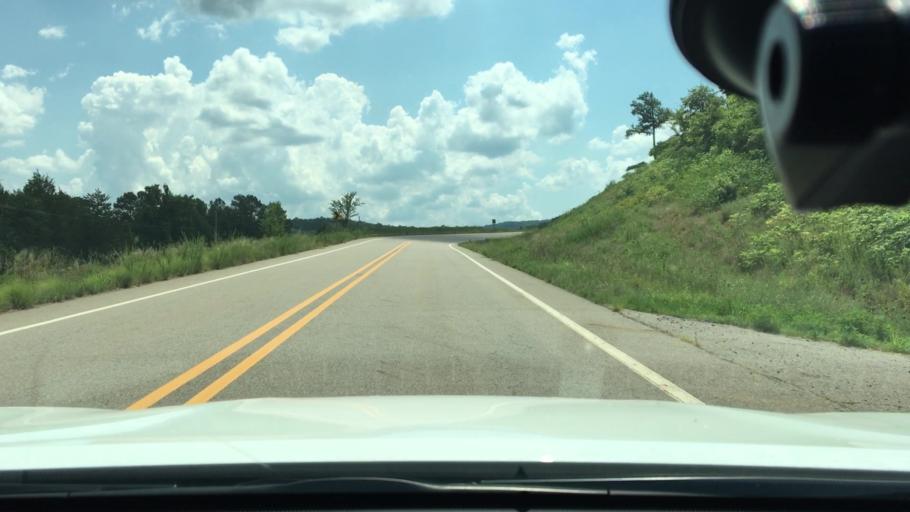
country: US
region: Arkansas
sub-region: Logan County
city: Paris
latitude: 35.2562
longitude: -93.6787
